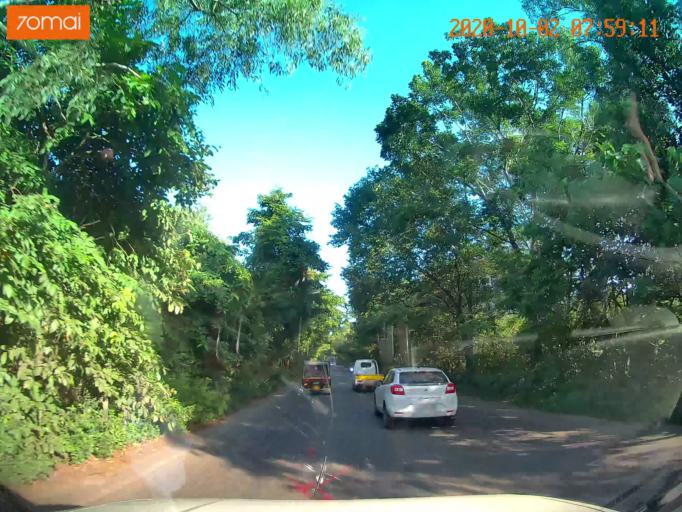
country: IN
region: Kerala
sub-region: Kozhikode
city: Ferokh
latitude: 11.2084
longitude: 75.8627
